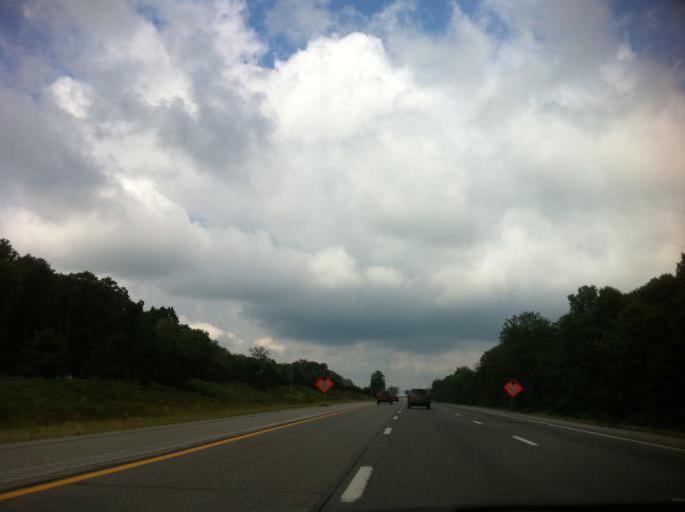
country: US
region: Ohio
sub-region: Summit County
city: Richfield
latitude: 41.2637
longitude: -81.6114
